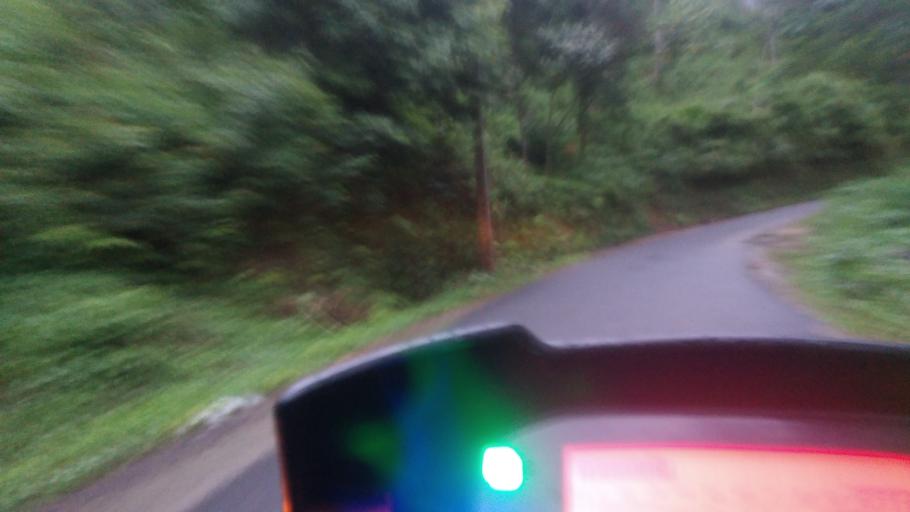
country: IN
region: Kerala
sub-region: Kottayam
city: Erattupetta
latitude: 9.5448
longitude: 76.9706
